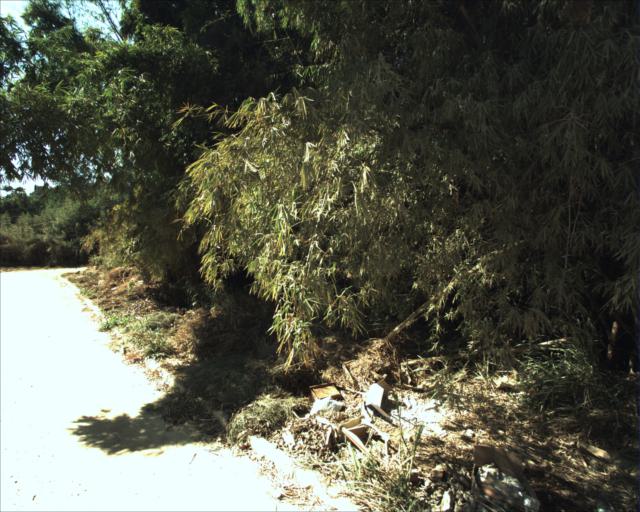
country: BR
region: Sao Paulo
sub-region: Sorocaba
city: Sorocaba
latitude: -23.4987
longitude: -47.4166
